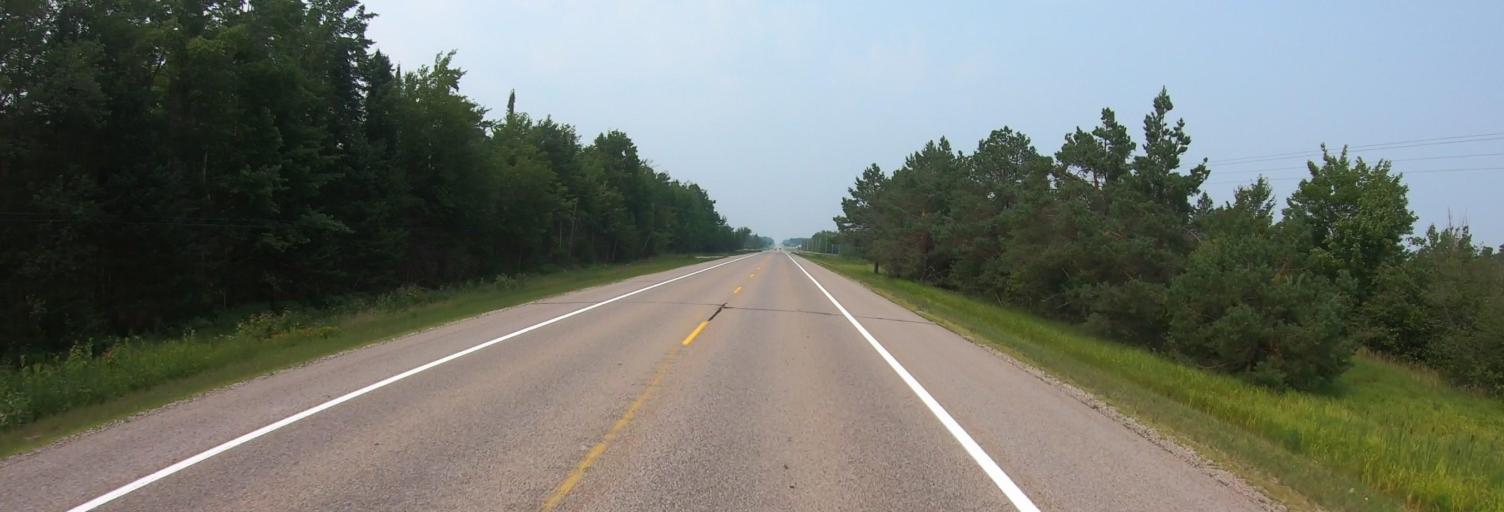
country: US
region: Michigan
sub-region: Chippewa County
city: Sault Ste. Marie
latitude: 46.2700
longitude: -84.3635
